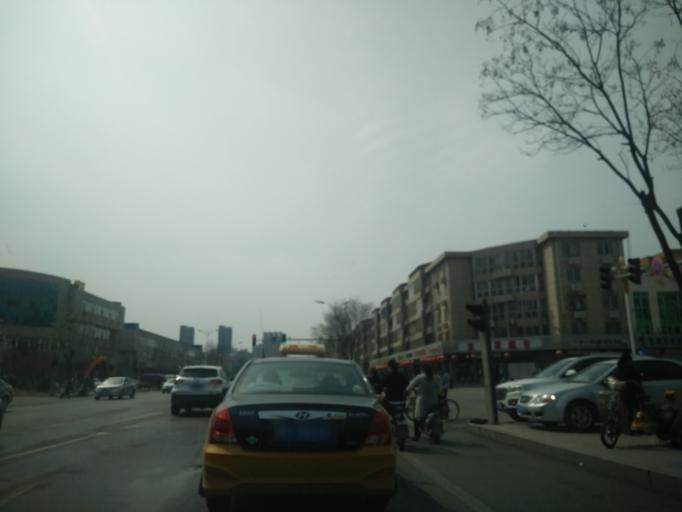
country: CN
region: Beijing
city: Xiji
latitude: 39.7632
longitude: 116.9995
